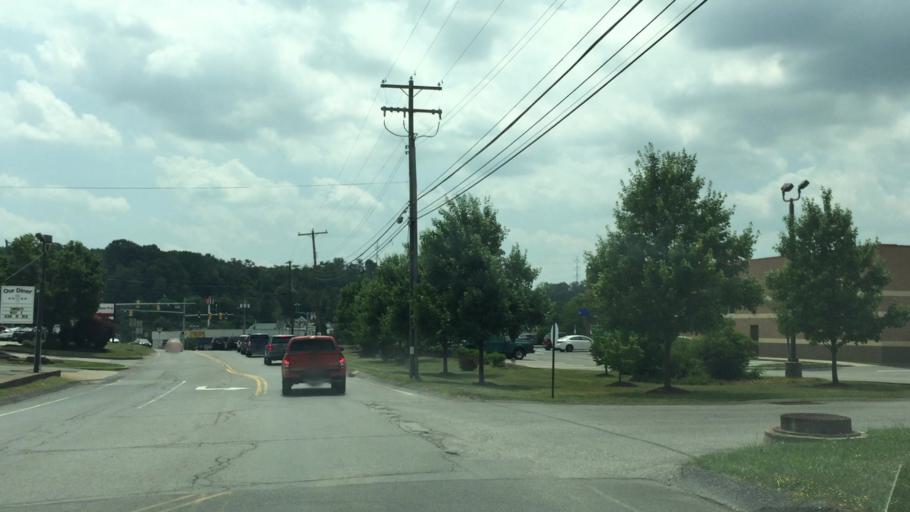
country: US
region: Pennsylvania
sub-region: Allegheny County
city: Imperial
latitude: 40.4429
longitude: -80.2383
